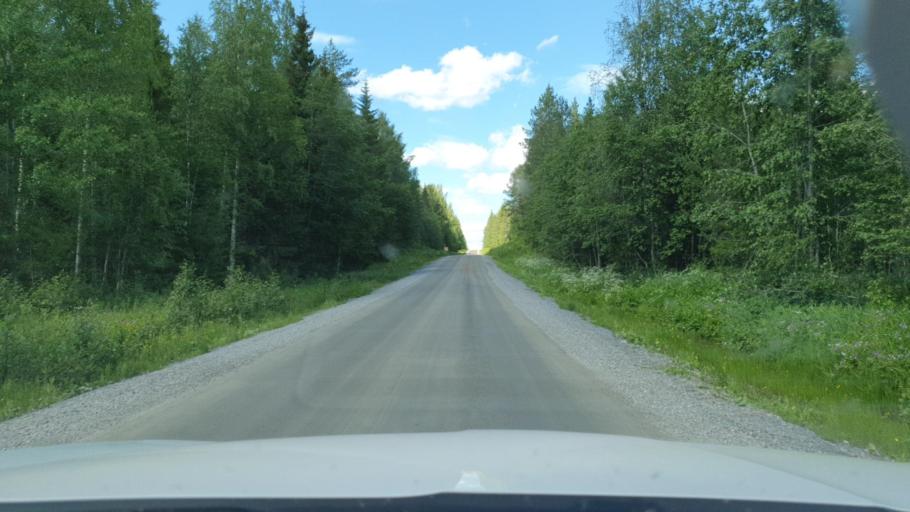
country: SE
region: Vaesterbotten
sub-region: Skelleftea Kommun
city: Forsbacka
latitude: 64.7939
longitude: 20.5071
